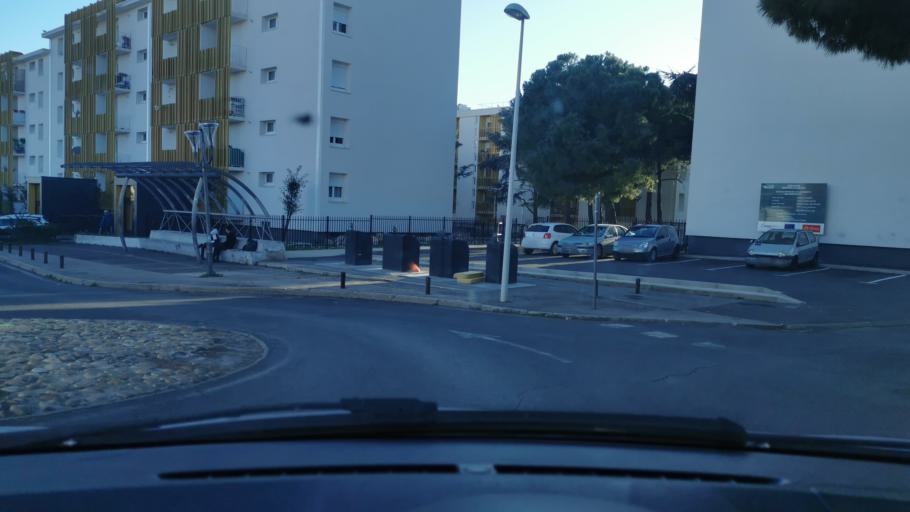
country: FR
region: Languedoc-Roussillon
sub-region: Departement de l'Herault
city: Frontignan
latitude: 43.4535
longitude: 3.7504
